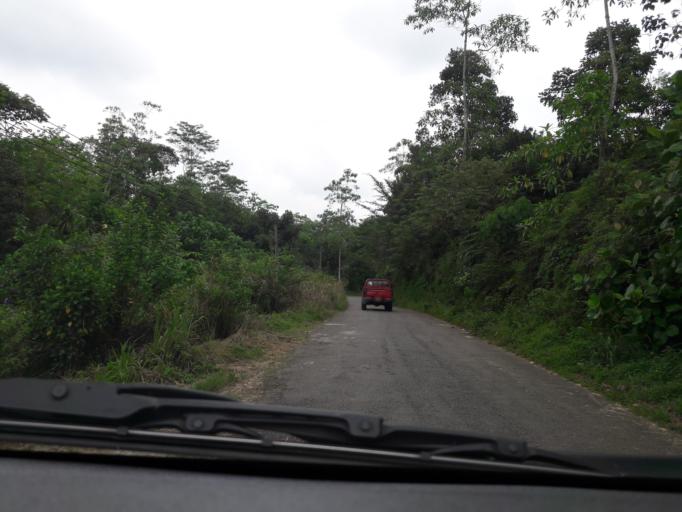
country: LK
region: Southern
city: Galle
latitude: 6.1872
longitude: 80.3044
